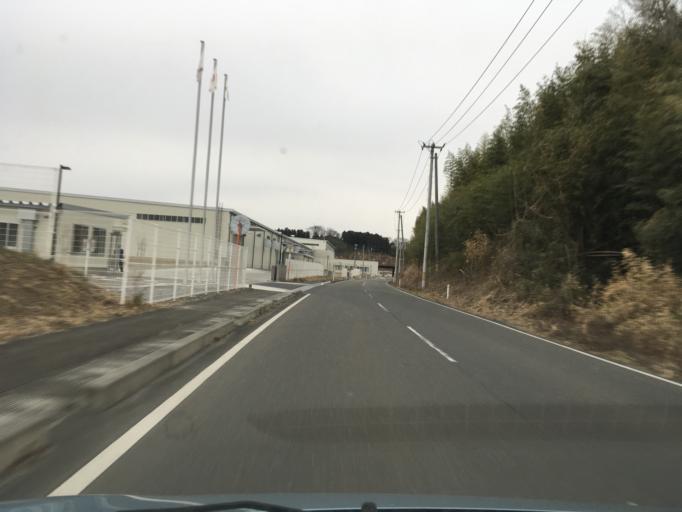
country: JP
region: Miyagi
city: Wakuya
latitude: 38.7014
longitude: 141.1684
